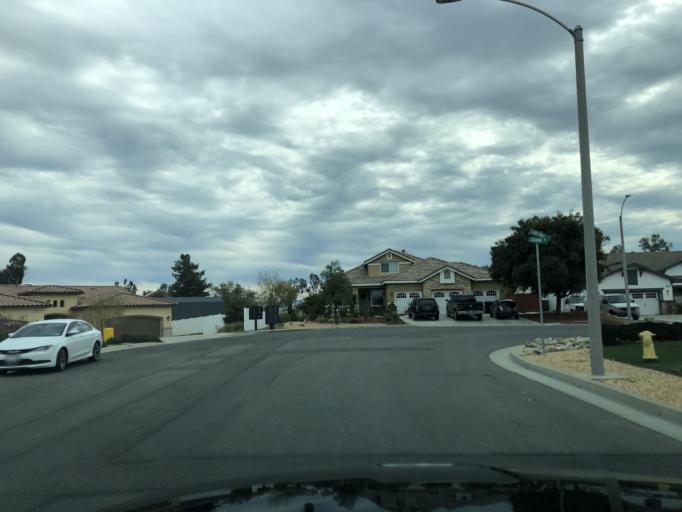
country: US
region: California
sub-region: Riverside County
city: Wildomar
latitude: 33.6132
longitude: -117.2770
